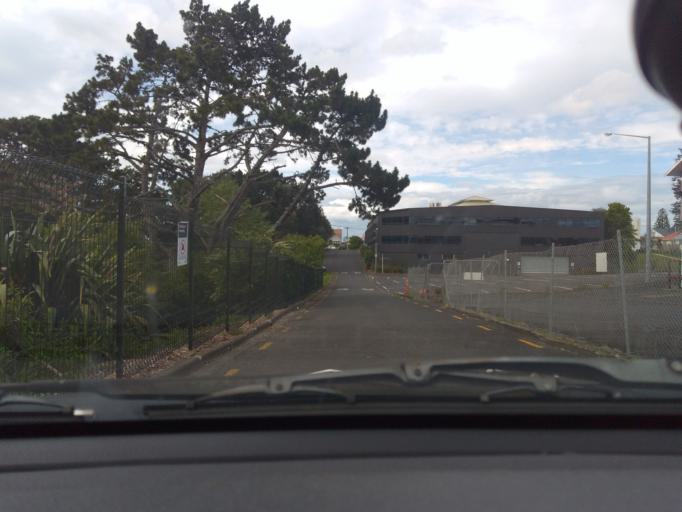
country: NZ
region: Auckland
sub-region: Auckland
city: Waitakere
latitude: -36.9082
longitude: 174.6807
